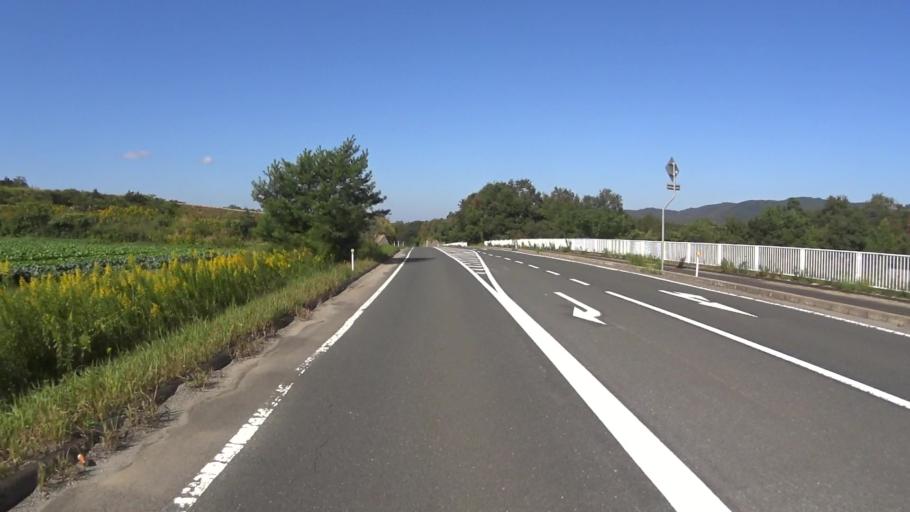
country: JP
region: Kyoto
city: Miyazu
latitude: 35.6680
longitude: 135.0991
